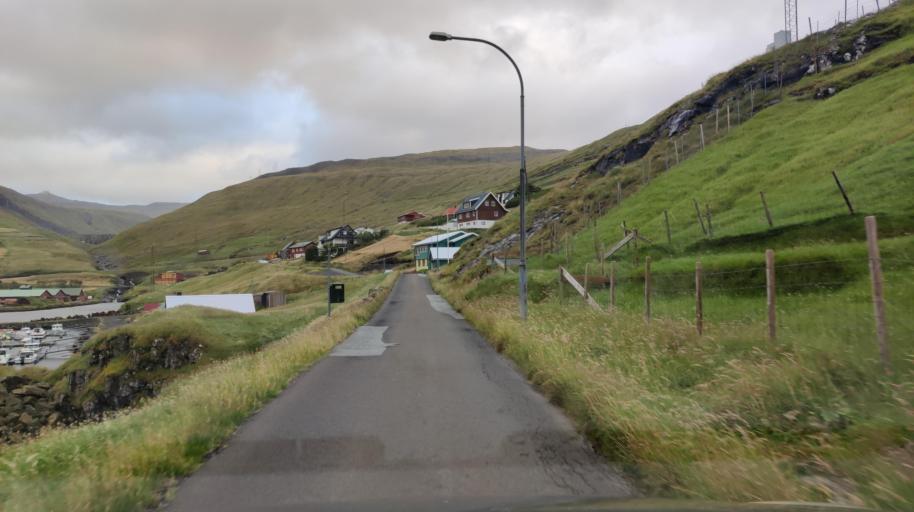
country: FO
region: Streymoy
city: Vestmanna
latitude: 62.1500
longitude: -7.1573
